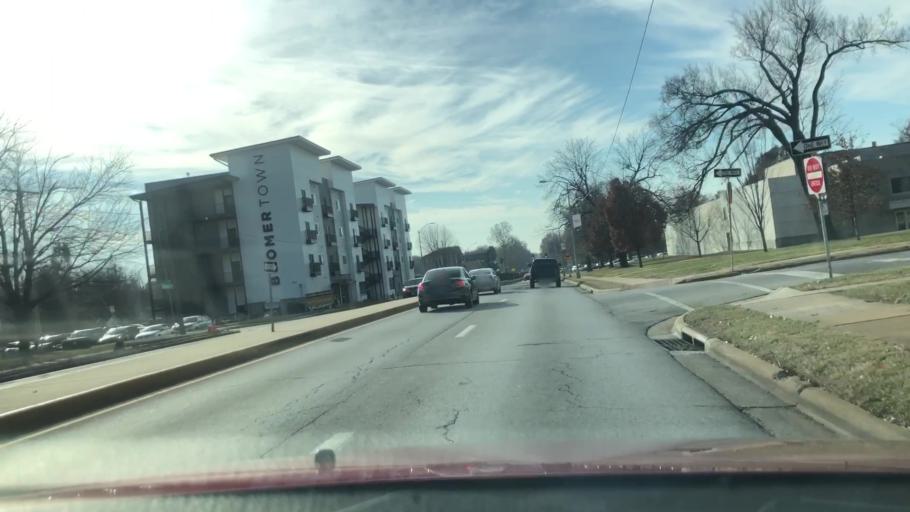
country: US
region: Missouri
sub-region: Greene County
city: Springfield
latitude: 37.2005
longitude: -93.2762
